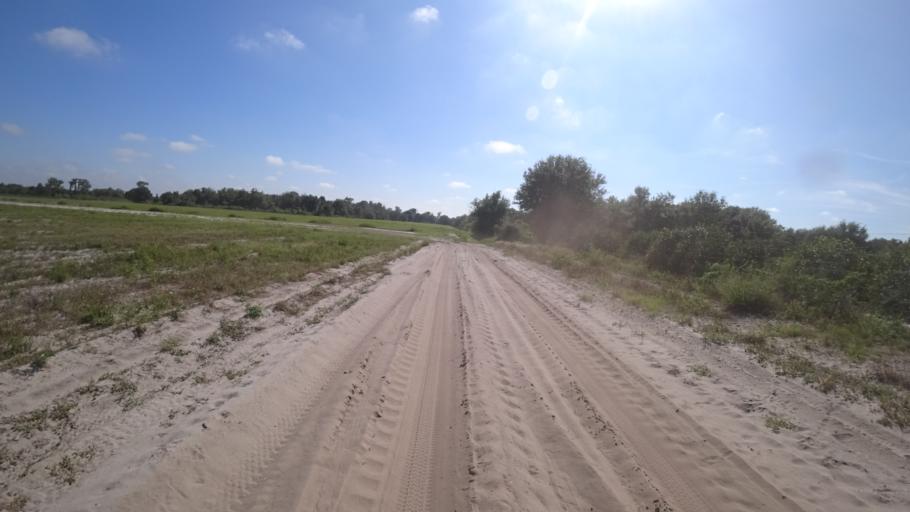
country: US
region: Florida
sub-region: DeSoto County
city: Arcadia
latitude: 27.2953
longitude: -82.0518
